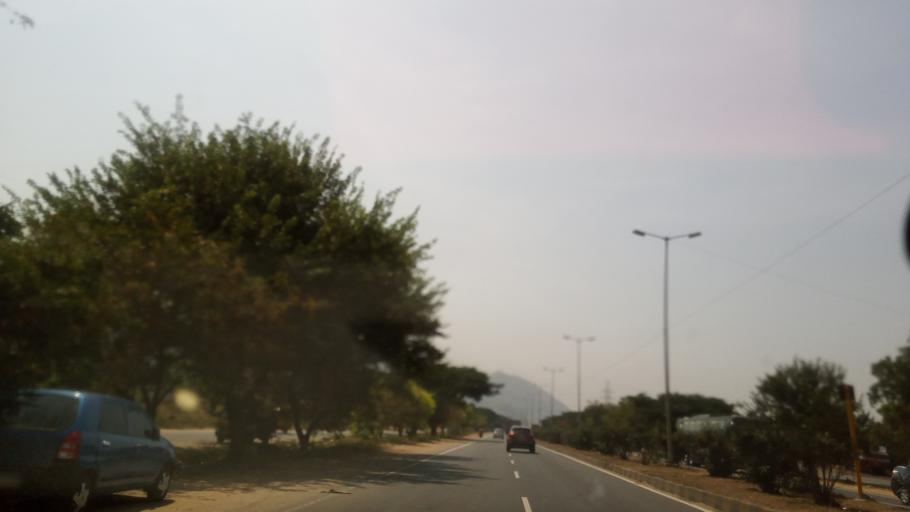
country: IN
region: Tamil Nadu
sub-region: Salem
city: Salem
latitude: 11.6423
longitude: 78.1763
